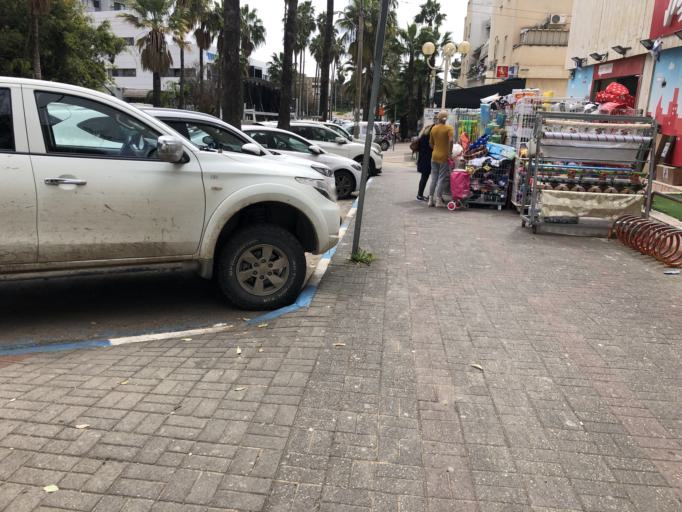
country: IL
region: Haifa
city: Hadera
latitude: 32.4739
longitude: 34.9734
